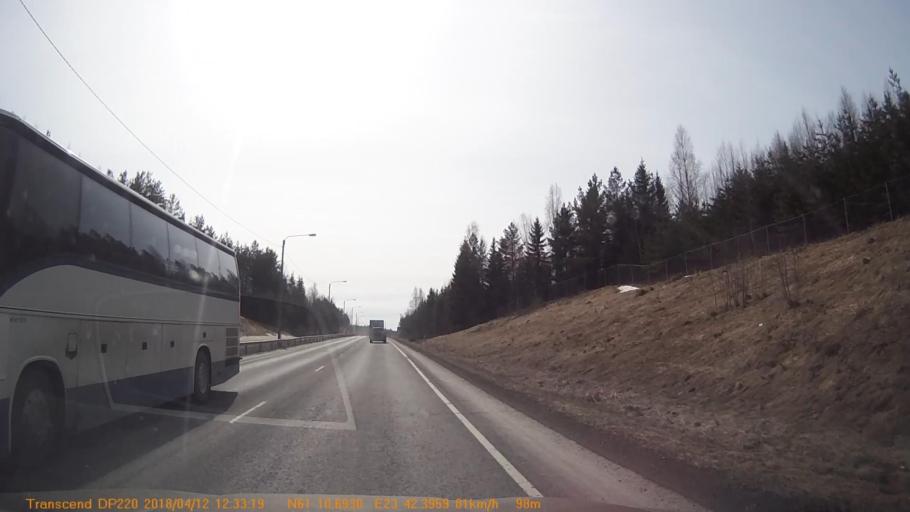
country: FI
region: Pirkanmaa
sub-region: Etelae-Pirkanmaa
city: Kylmaekoski
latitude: 61.1780
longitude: 23.7065
